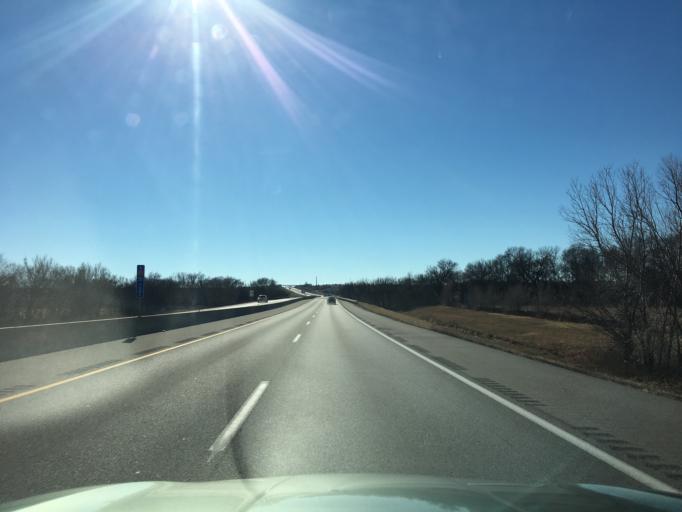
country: US
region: Kansas
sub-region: Sumner County
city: Wellington
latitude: 37.2190
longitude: -97.3390
